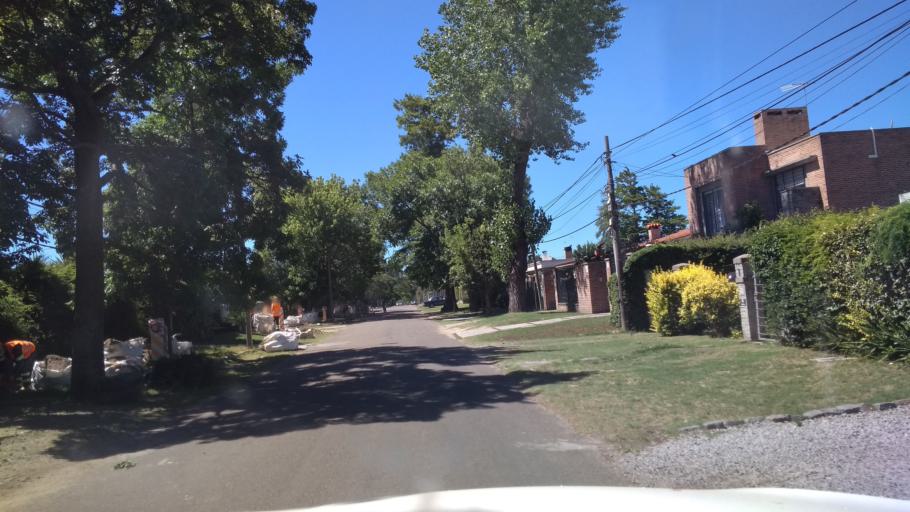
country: UY
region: Canelones
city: Paso de Carrasco
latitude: -34.8721
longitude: -56.0612
